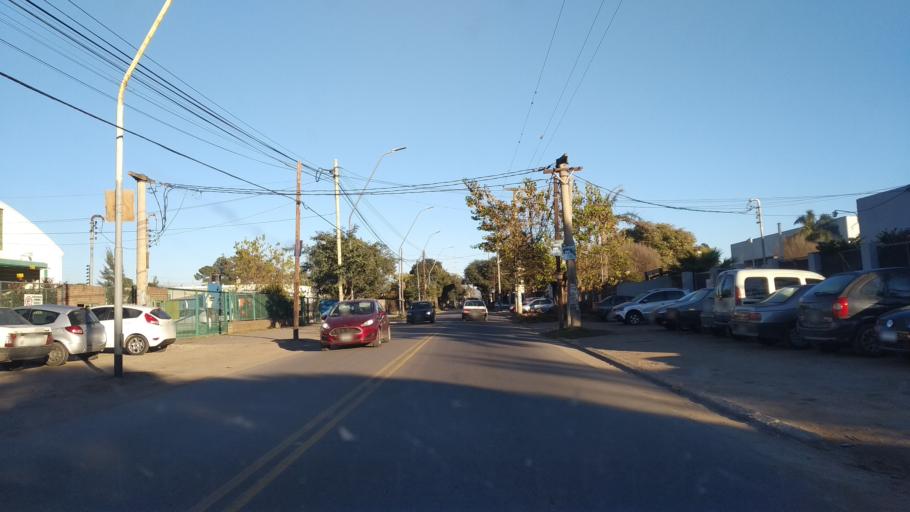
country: AR
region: Cordoba
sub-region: Departamento de Capital
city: Cordoba
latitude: -31.3433
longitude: -64.2143
